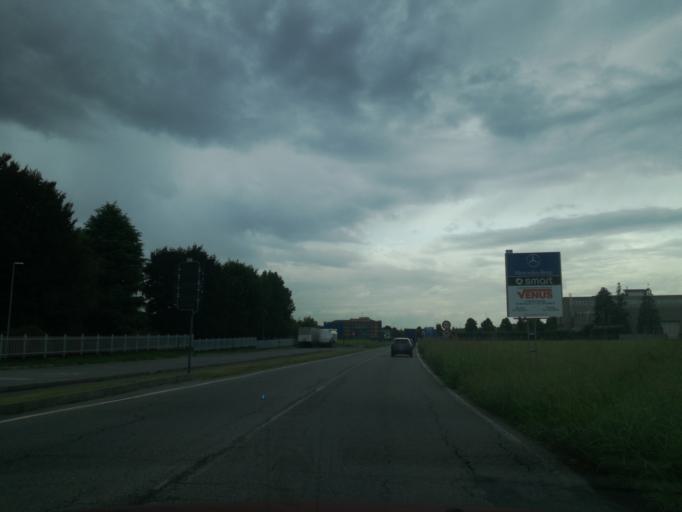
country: IT
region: Lombardy
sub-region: Provincia di Monza e Brianza
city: Ornago
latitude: 45.6073
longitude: 9.4194
